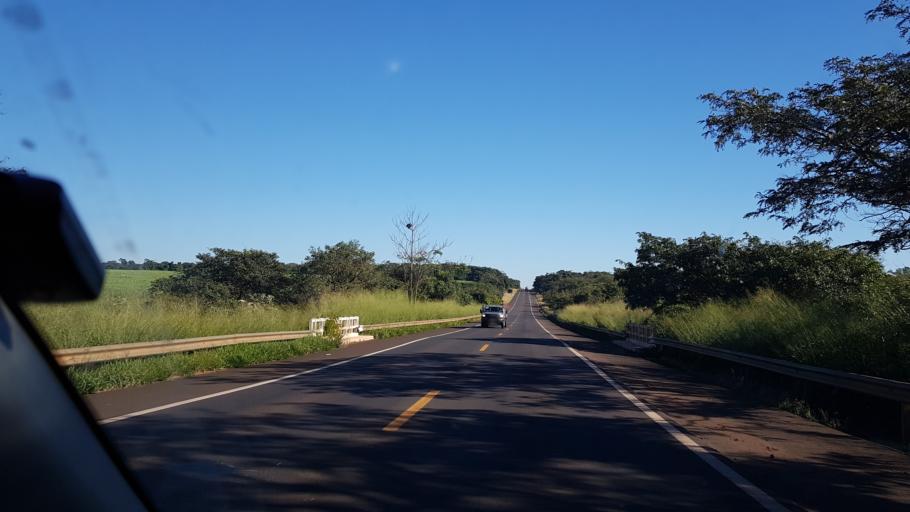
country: BR
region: Sao Paulo
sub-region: Assis
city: Assis
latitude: -22.5902
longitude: -50.4937
